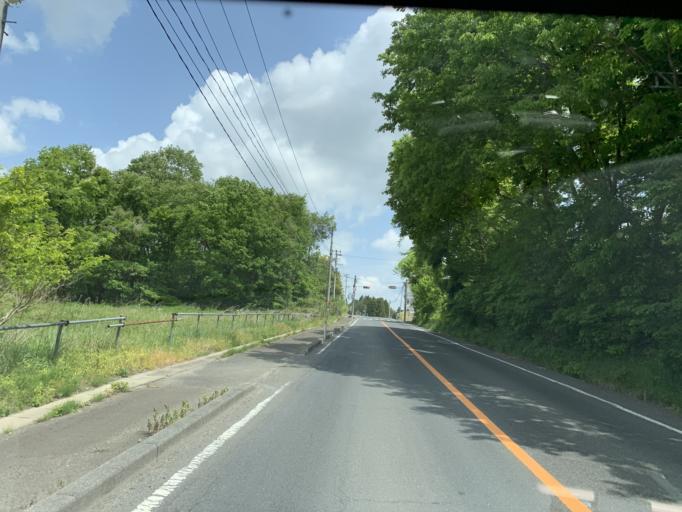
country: JP
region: Miyagi
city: Kogota
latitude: 38.6577
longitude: 141.0605
